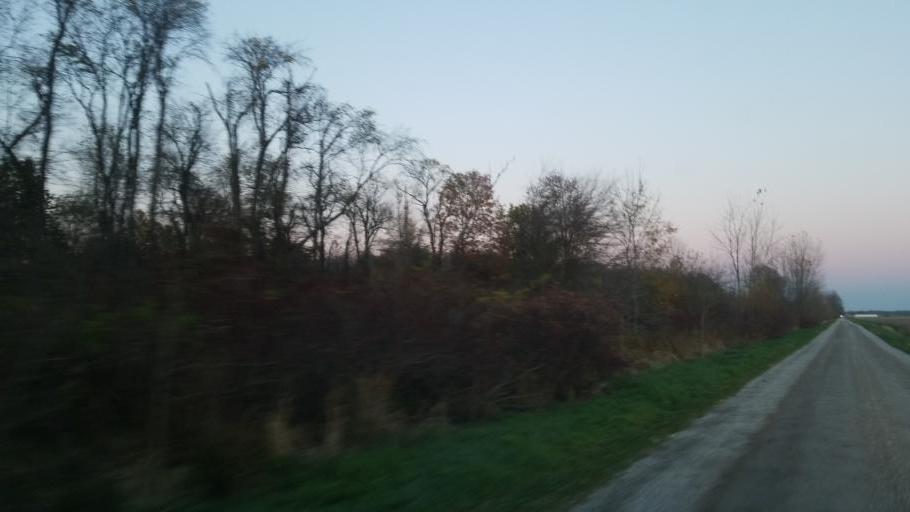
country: US
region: Ohio
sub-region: Huron County
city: Willard
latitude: 40.9959
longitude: -82.7713
